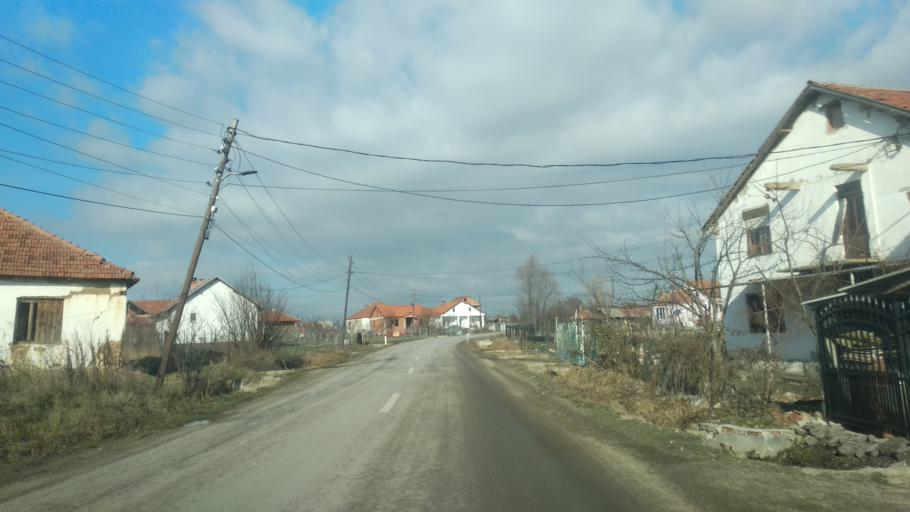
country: XK
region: Pristina
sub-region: Lipjan
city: Lipljan
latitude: 42.5658
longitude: 21.1642
